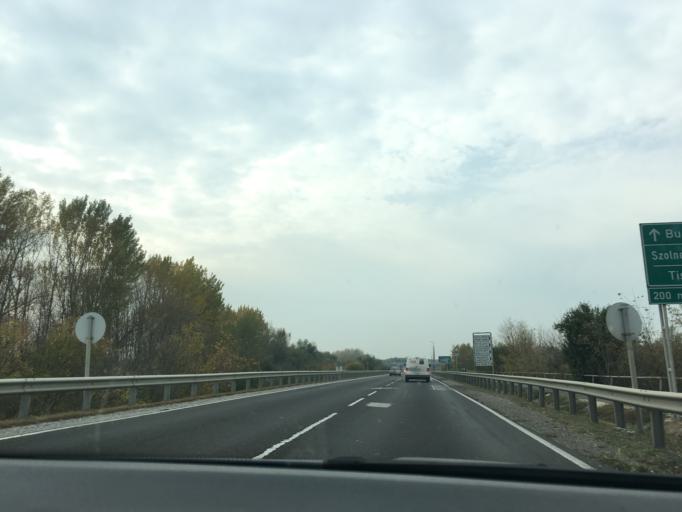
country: HU
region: Jasz-Nagykun-Szolnok
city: Szolnok
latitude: 47.1447
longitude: 20.1705
